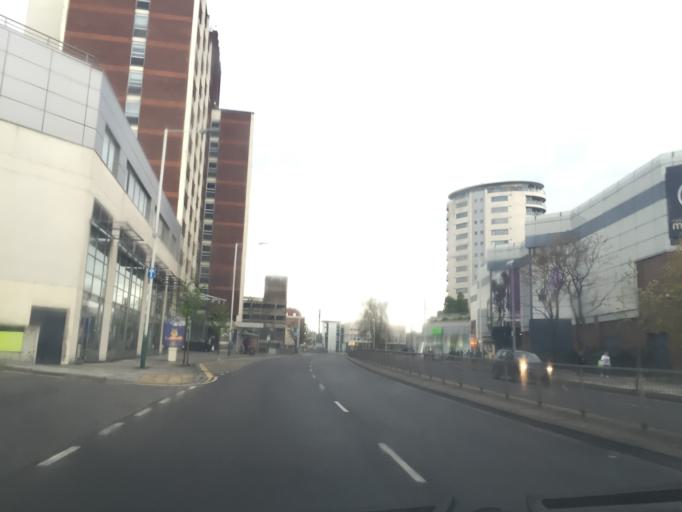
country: GB
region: England
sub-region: Greater London
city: Romford
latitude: 51.5785
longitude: 0.1855
